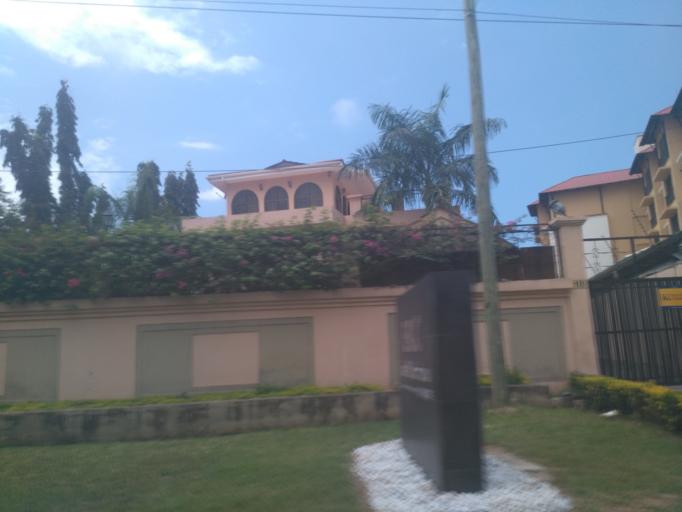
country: TZ
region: Dar es Salaam
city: Magomeni
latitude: -6.7564
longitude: 39.2786
